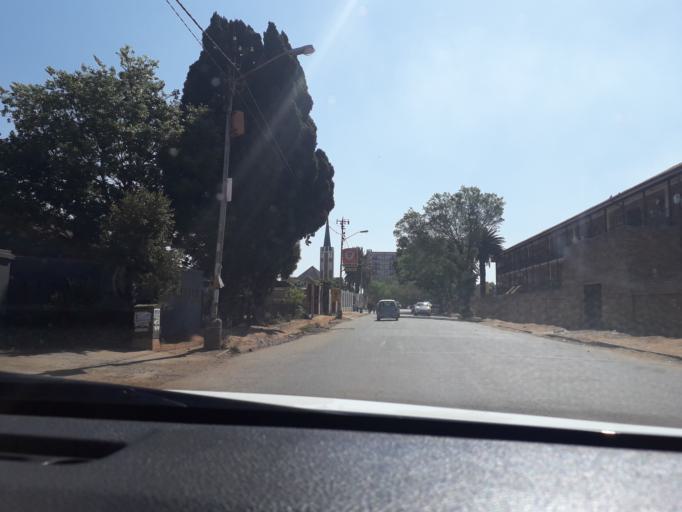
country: ZA
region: Gauteng
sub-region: City of Johannesburg Metropolitan Municipality
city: Modderfontein
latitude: -26.1039
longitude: 28.2338
